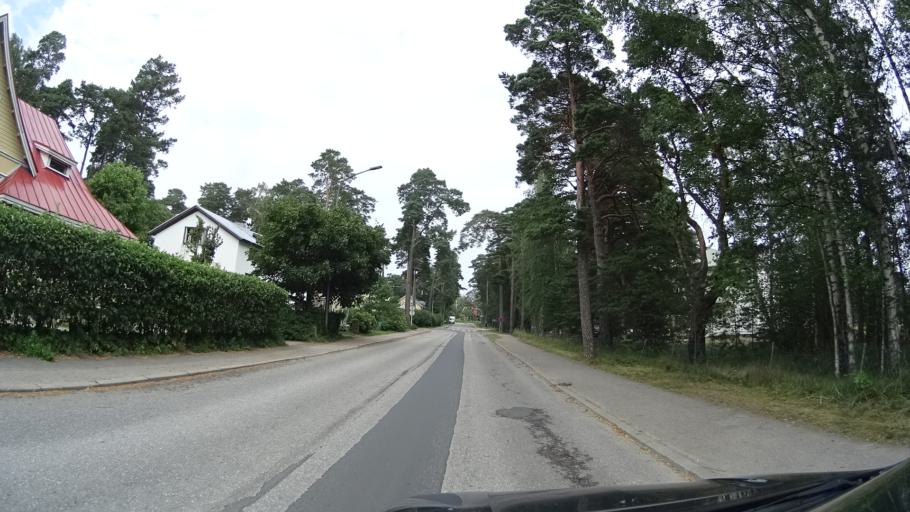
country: FI
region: Uusimaa
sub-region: Raaseporin
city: Hanko
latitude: 59.8276
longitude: 22.9874
